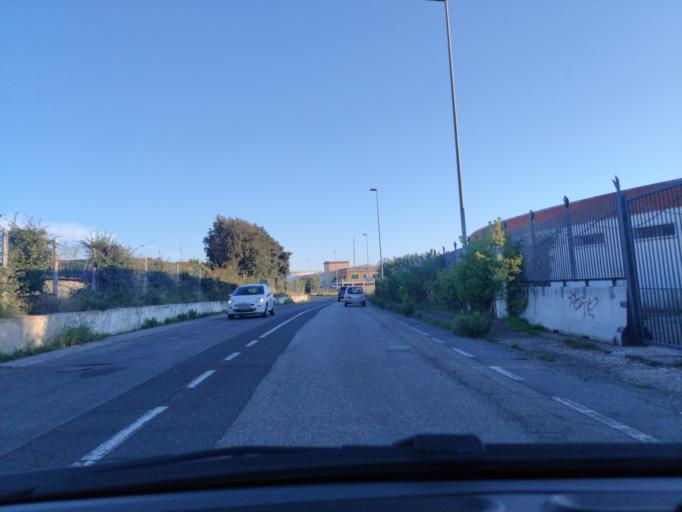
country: IT
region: Latium
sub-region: Citta metropolitana di Roma Capitale
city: Civitavecchia
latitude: 42.1101
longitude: 11.7775
